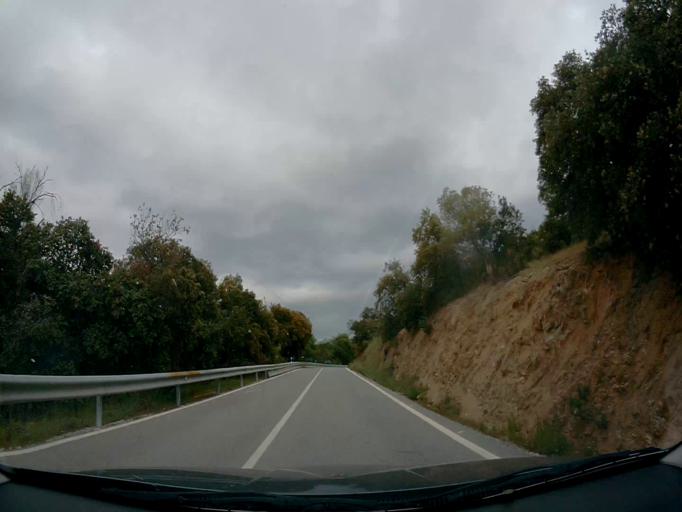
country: ES
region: Madrid
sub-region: Provincia de Madrid
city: Navalagamella
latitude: 40.4364
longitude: -4.1099
